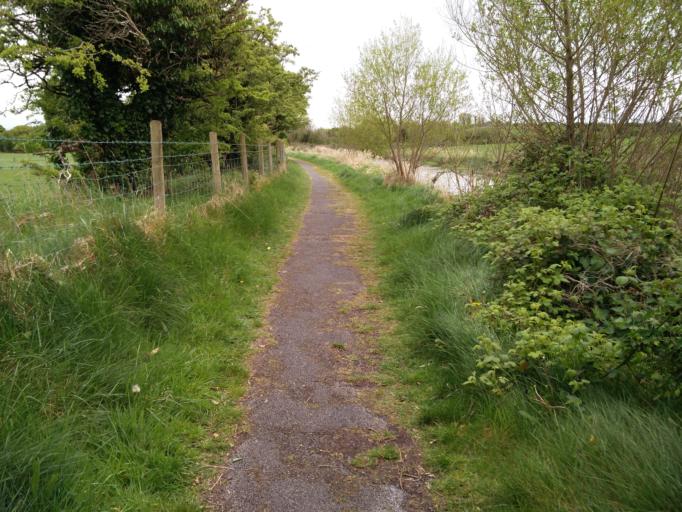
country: IE
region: Connaught
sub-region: Maigh Eo
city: Ballinrobe
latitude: 53.6244
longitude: -9.2405
